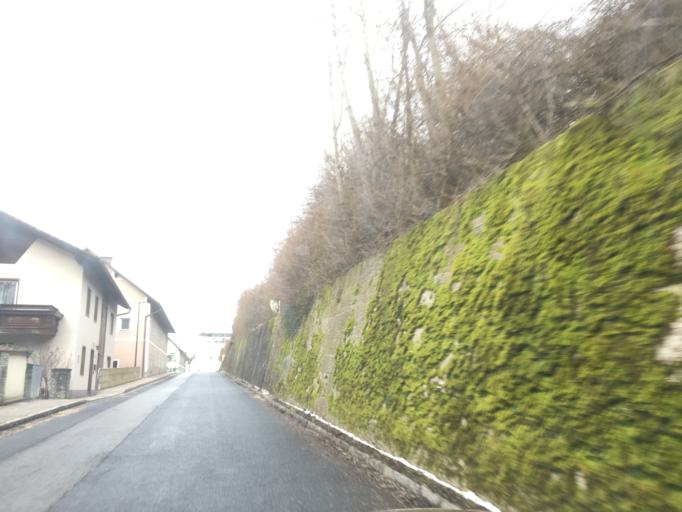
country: AT
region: Upper Austria
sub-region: Politischer Bezirk Kirchdorf an der Krems
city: Micheldorf in Oberoesterreich
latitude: 47.9350
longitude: 14.1255
